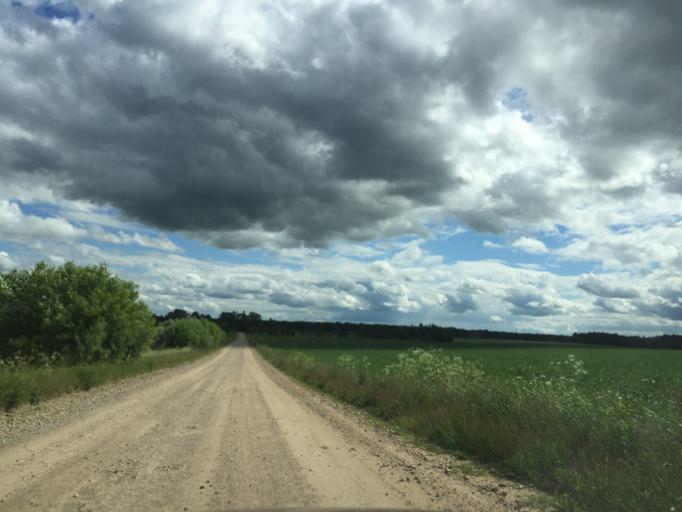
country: LV
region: Vecumnieki
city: Vecumnieki
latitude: 56.4781
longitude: 24.4170
